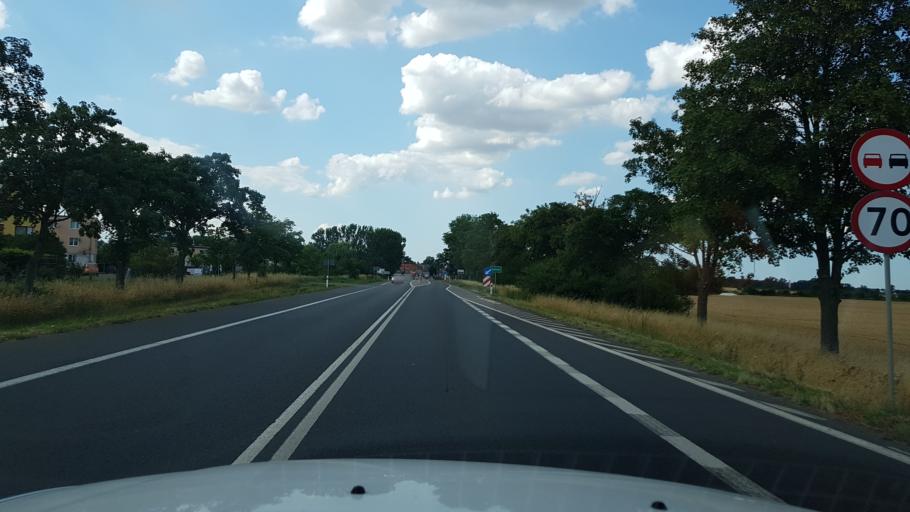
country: PL
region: West Pomeranian Voivodeship
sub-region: Powiat pyrzycki
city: Pyrzyce
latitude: 53.1799
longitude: 14.8443
